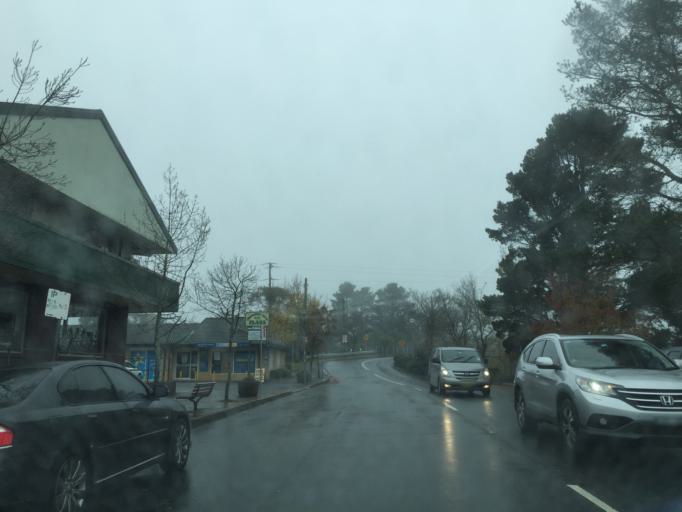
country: AU
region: New South Wales
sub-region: Blue Mountains Municipality
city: Leura
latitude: -33.7089
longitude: 150.3759
